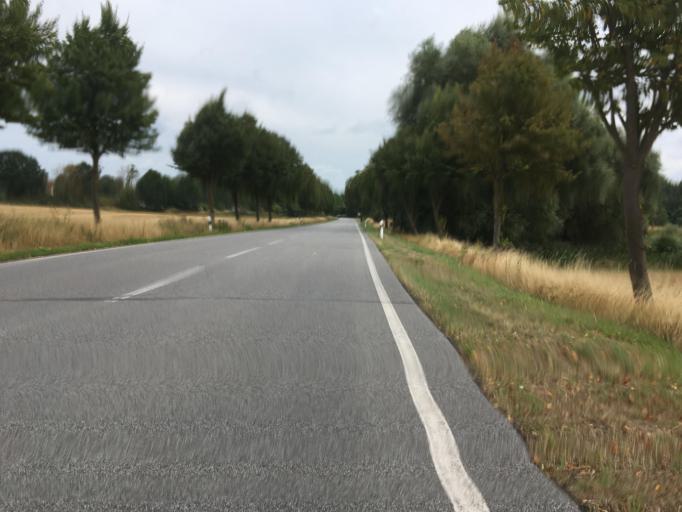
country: DE
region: Brandenburg
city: Zichow
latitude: 53.1961
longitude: 14.0341
